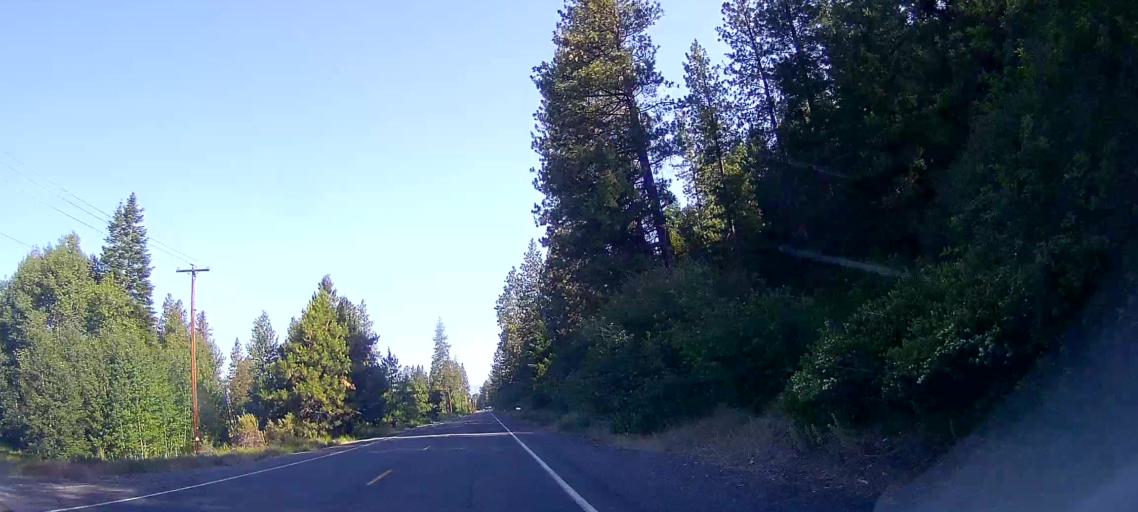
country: US
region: Oregon
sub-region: Klamath County
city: Klamath Falls
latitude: 42.6364
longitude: -121.9394
